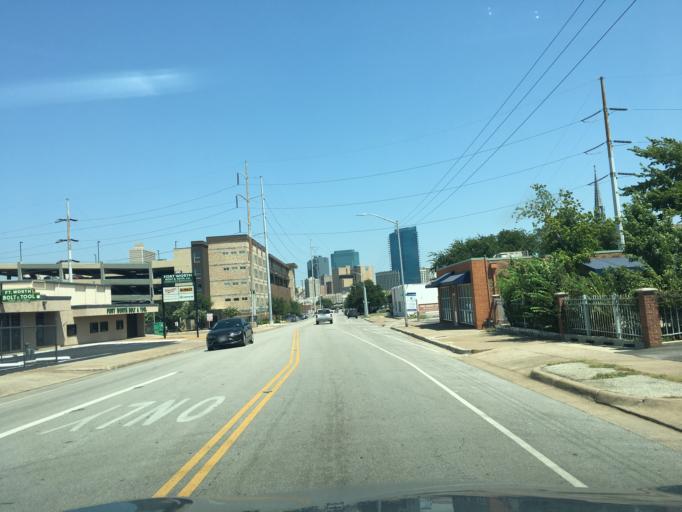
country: US
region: Texas
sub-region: Tarrant County
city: Fort Worth
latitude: 32.7383
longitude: -97.3298
